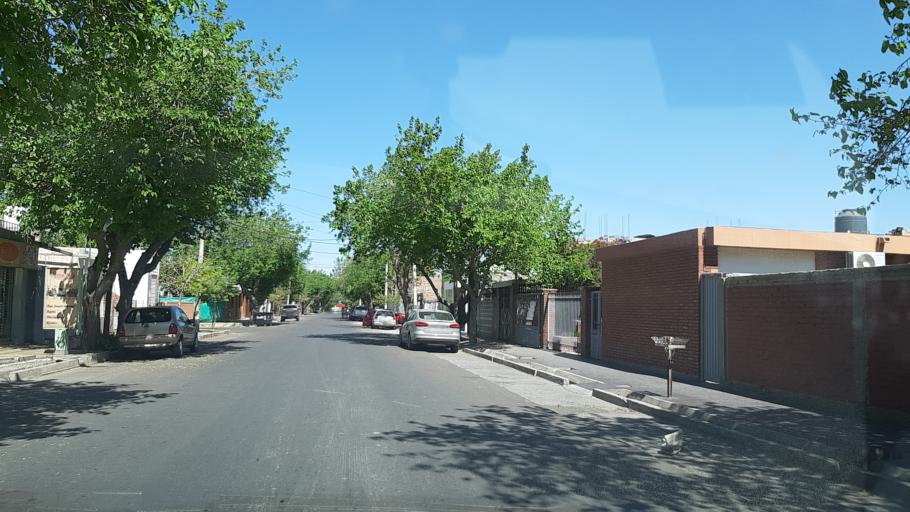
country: AR
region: San Juan
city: San Juan
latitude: -31.5282
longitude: -68.5489
